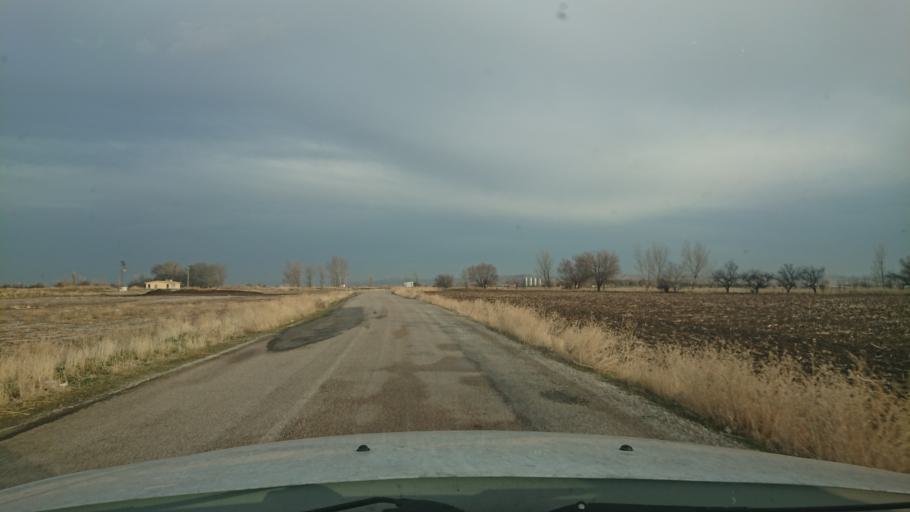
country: TR
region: Aksaray
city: Yesilova
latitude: 38.4445
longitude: 33.8368
